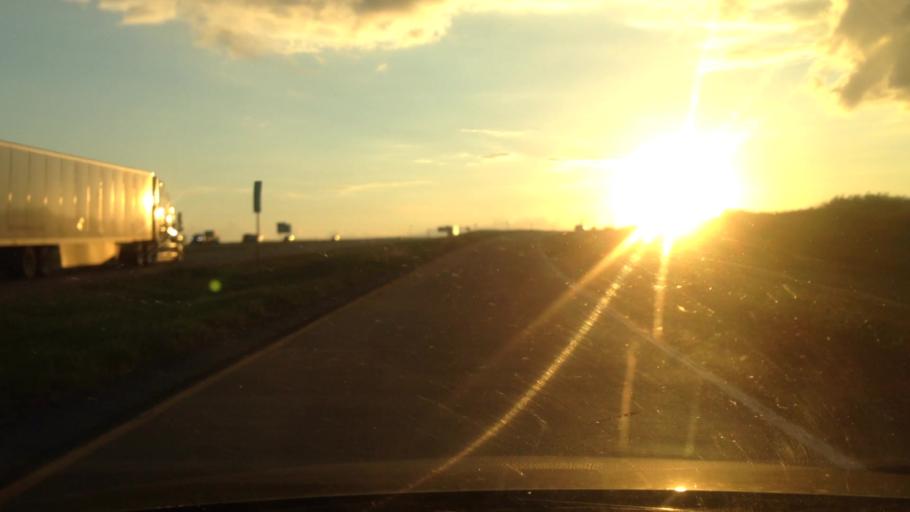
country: US
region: Texas
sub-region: Tarrant County
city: Benbrook
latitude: 32.6936
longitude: -97.4930
